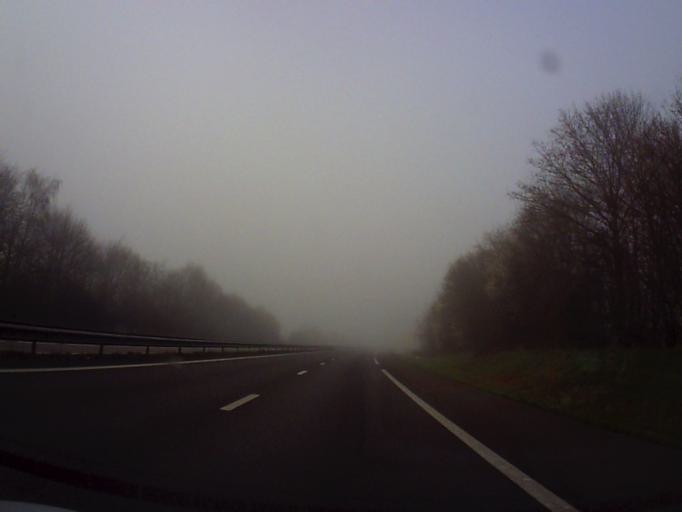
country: FR
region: Brittany
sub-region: Departement d'Ille-et-Vilaine
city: Chavagne
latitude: 48.0758
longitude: -1.7994
